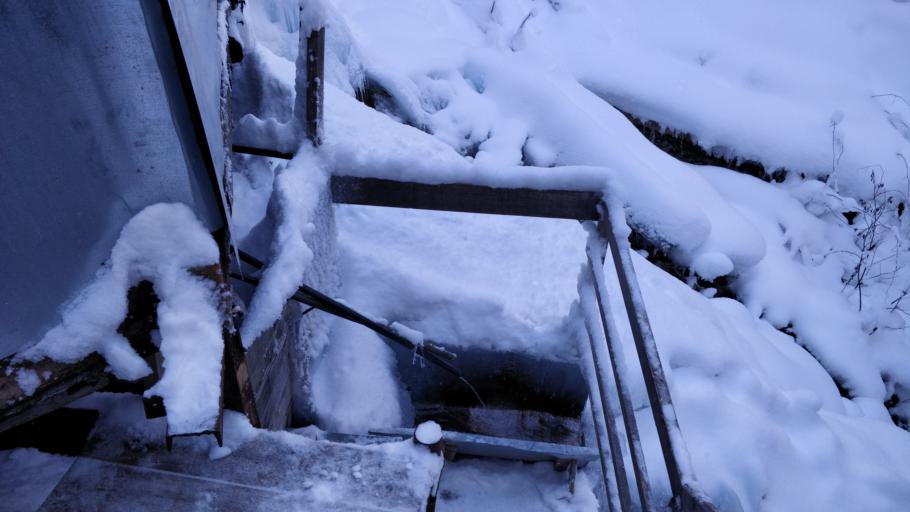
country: RU
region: Perm
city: Verkhnechusovskiye Gorodki
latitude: 58.2126
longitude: 57.0721
